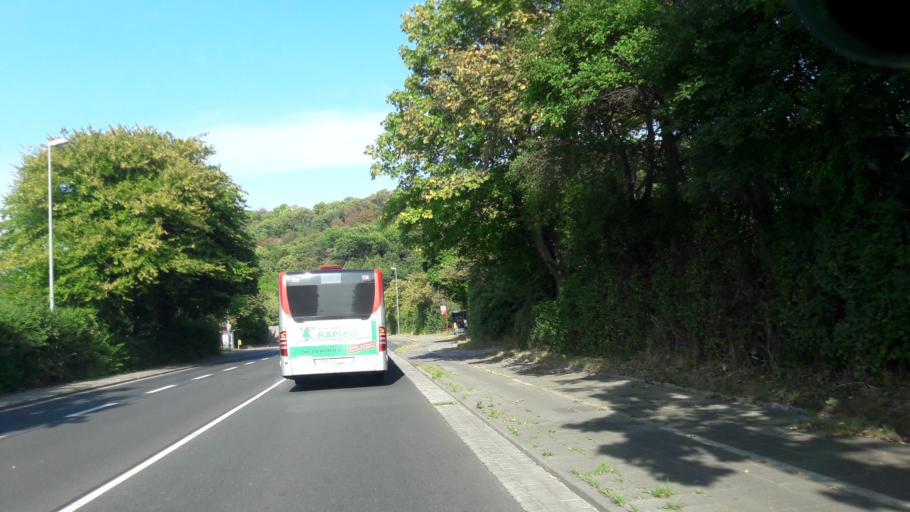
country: DE
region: Lower Saxony
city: Hildesheim
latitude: 52.1320
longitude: 9.9273
